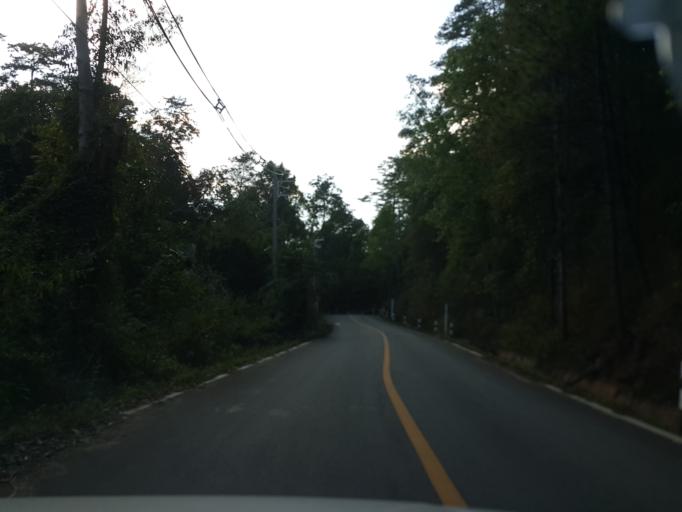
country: TH
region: Chiang Mai
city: Mae Wang
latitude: 18.6830
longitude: 98.5566
